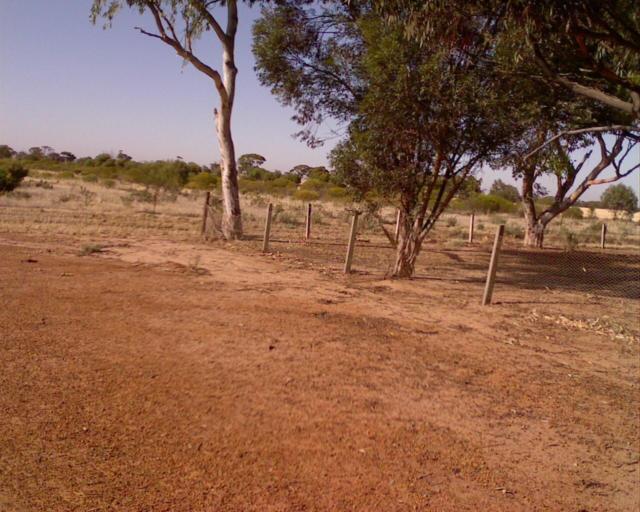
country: AU
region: Western Australia
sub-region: Merredin
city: Merredin
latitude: -31.1108
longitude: 117.7864
